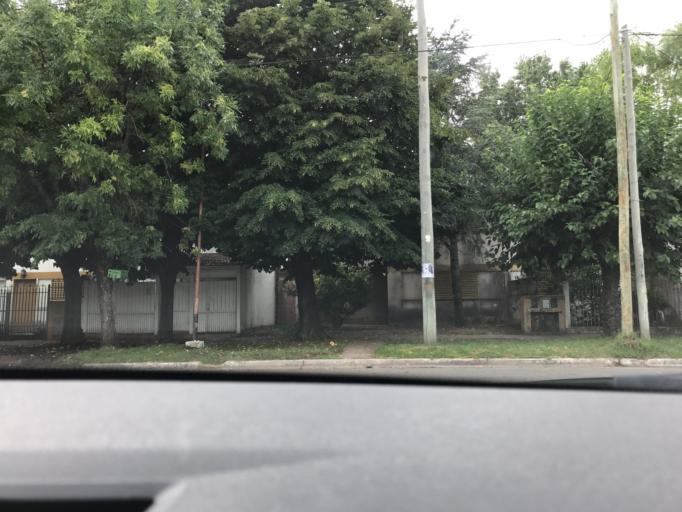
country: AR
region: Buenos Aires
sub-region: Partido de La Plata
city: La Plata
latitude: -34.8486
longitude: -58.0789
